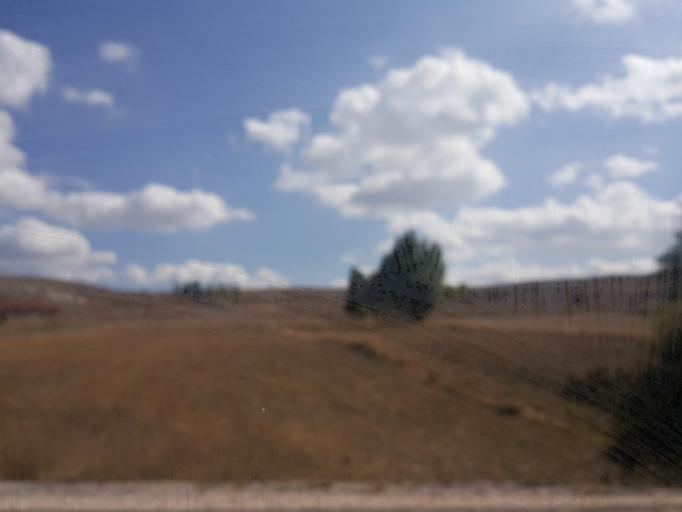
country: TR
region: Tokat
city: Artova
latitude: 40.1388
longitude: 36.3573
